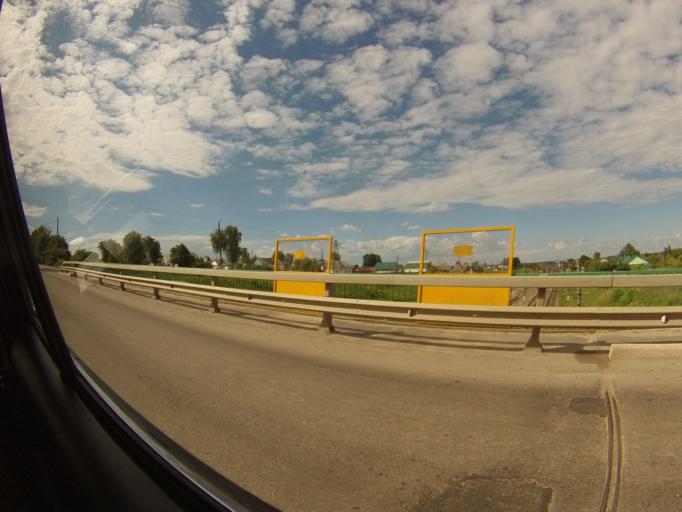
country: RU
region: Orjol
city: Mtsensk
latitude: 53.2849
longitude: 36.5603
